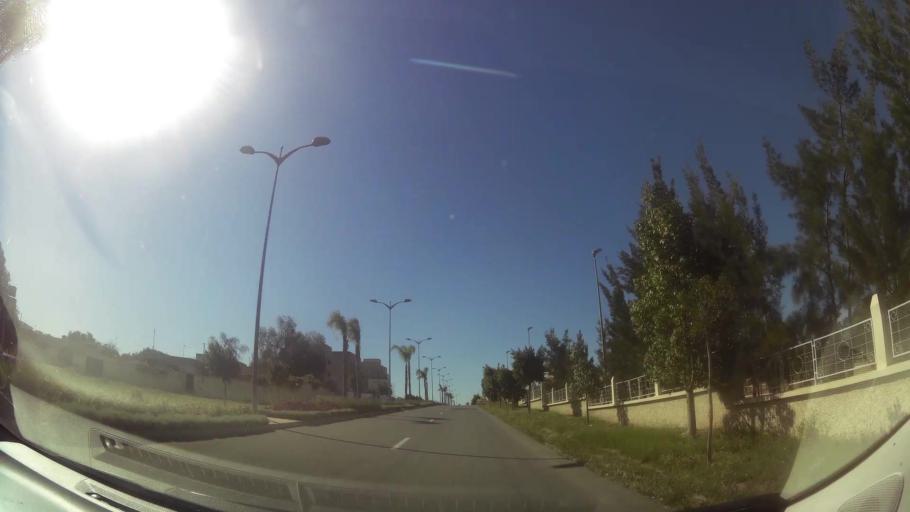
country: MA
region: Oriental
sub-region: Oujda-Angad
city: Oujda
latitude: 34.7248
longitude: -1.9121
